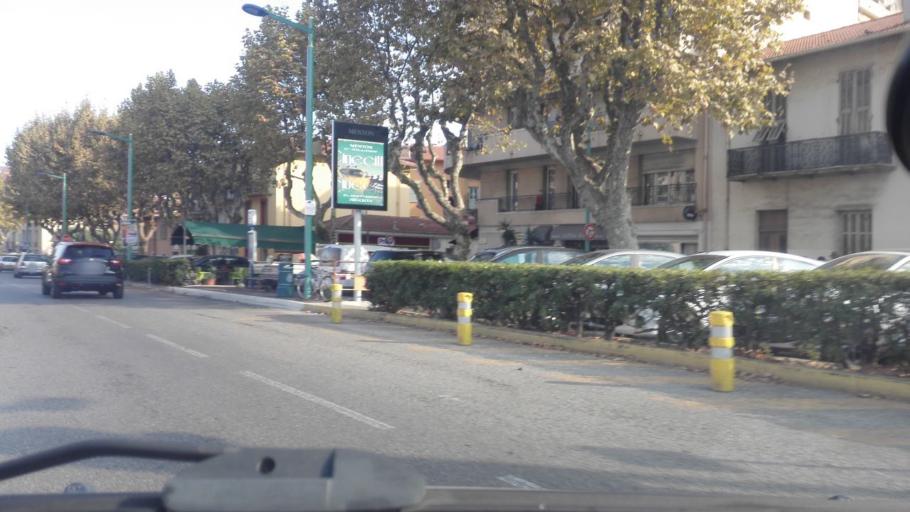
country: FR
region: Provence-Alpes-Cote d'Azur
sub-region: Departement des Alpes-Maritimes
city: Roquebrune-Cap-Martin
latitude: 43.7722
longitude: 7.4917
